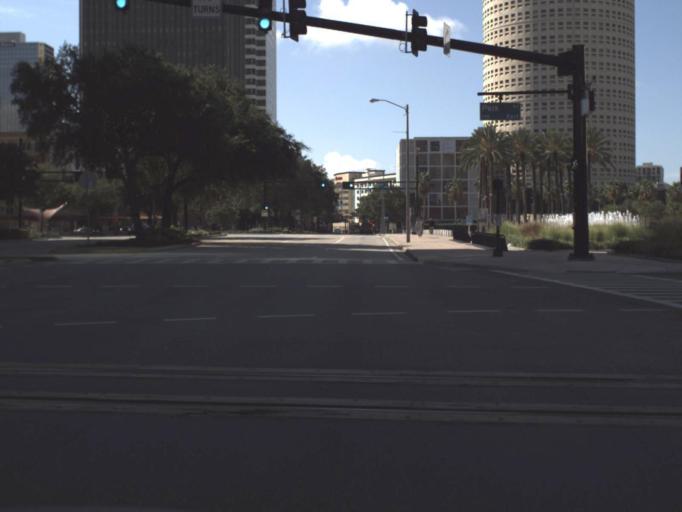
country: US
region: Florida
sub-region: Hillsborough County
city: Tampa
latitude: 27.9501
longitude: -82.4612
